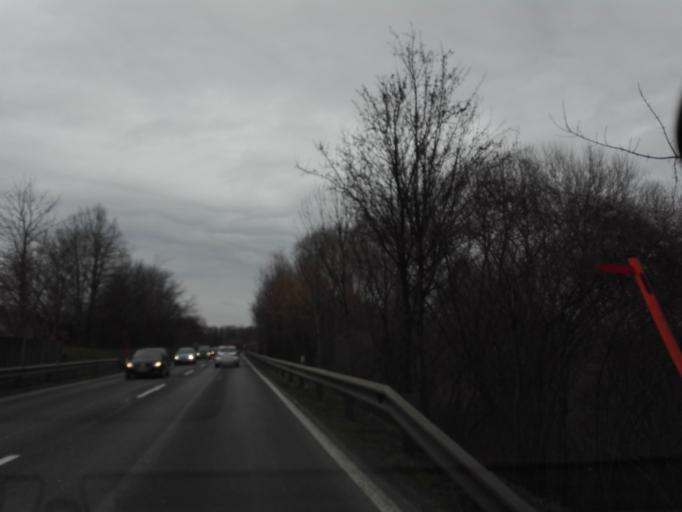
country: AT
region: Upper Austria
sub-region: Politischer Bezirk Linz-Land
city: Ansfelden
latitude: 48.2158
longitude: 14.2670
